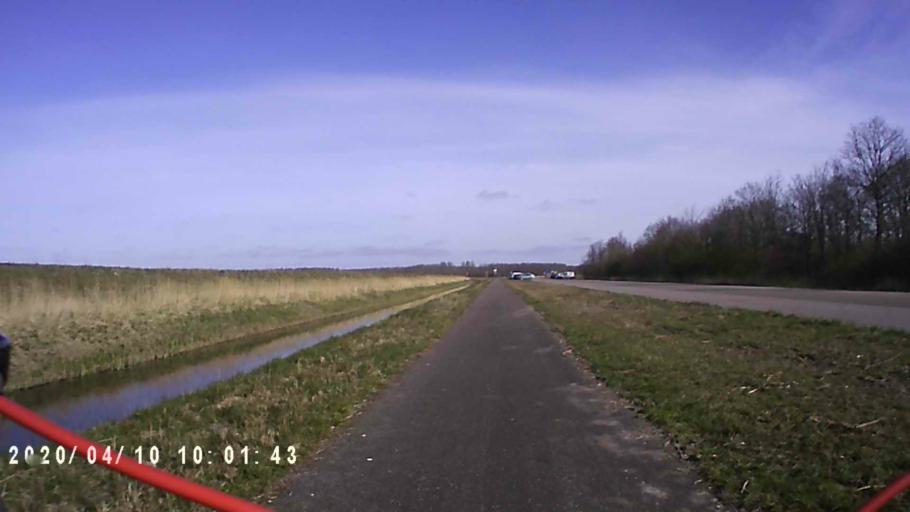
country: NL
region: Groningen
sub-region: Gemeente De Marne
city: Ulrum
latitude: 53.3625
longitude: 6.2606
